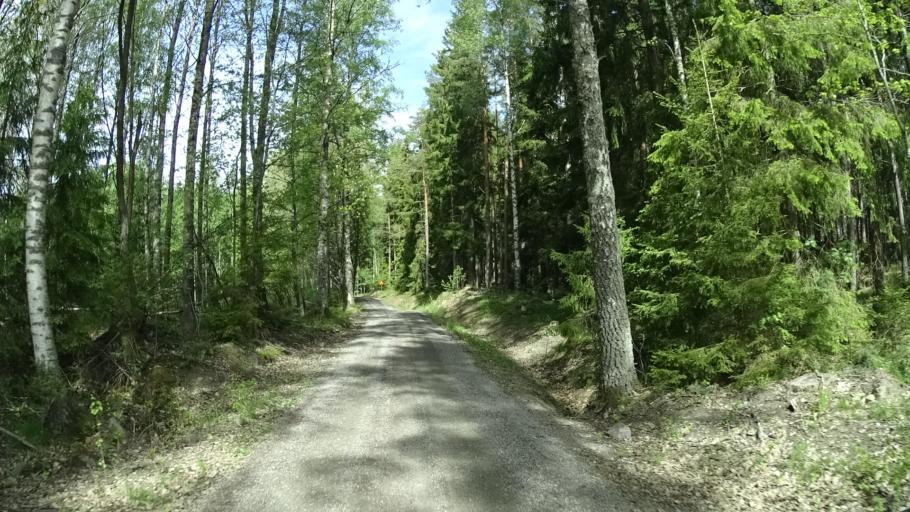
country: SE
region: OEstergoetland
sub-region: Finspangs Kommun
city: Finspang
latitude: 58.7896
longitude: 15.8713
